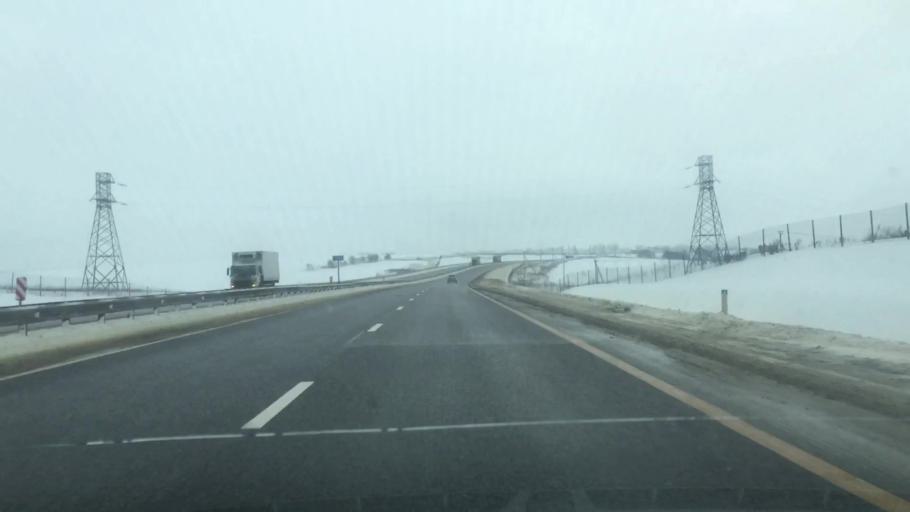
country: RU
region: Tula
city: Yefremov
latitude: 53.1443
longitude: 38.2479
